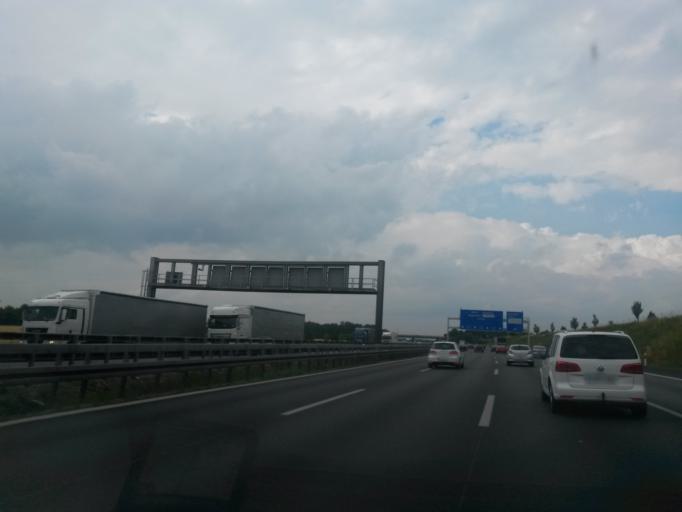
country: DE
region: Bavaria
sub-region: Upper Bavaria
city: Garching bei Munchen
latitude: 48.2592
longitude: 11.6474
